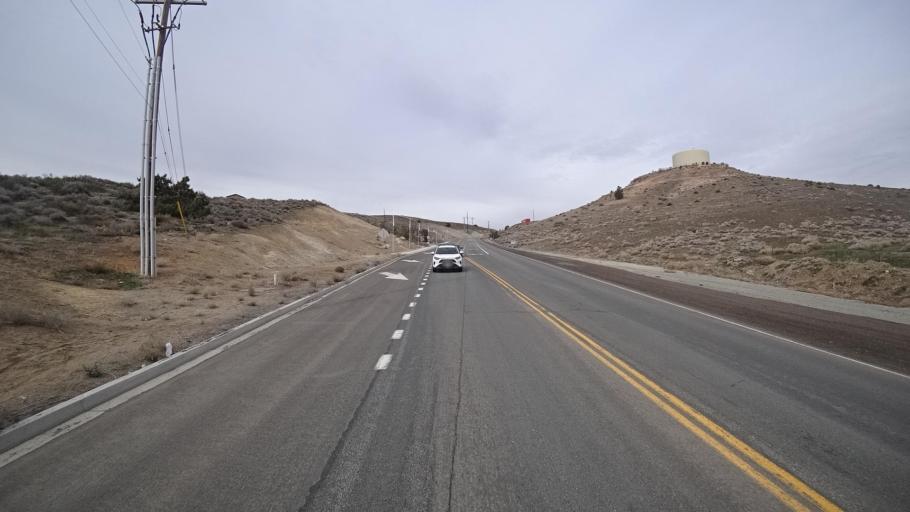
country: US
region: Nevada
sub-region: Washoe County
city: Golden Valley
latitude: 39.6013
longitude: -119.8046
